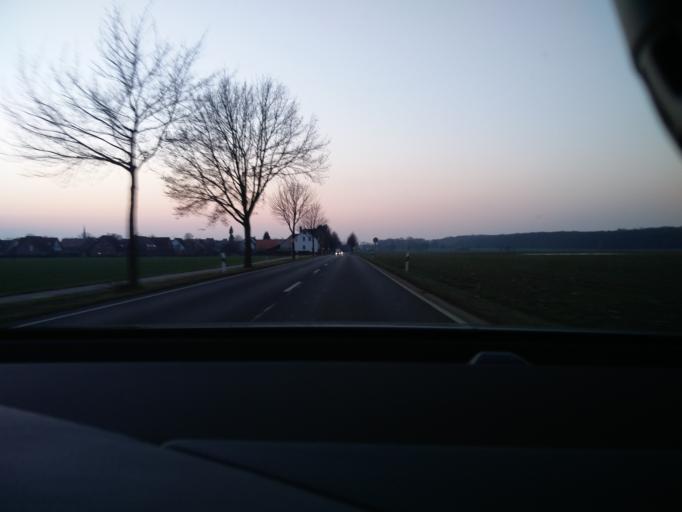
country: DE
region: Lower Saxony
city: Sehnde
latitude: 52.3204
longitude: 9.9412
